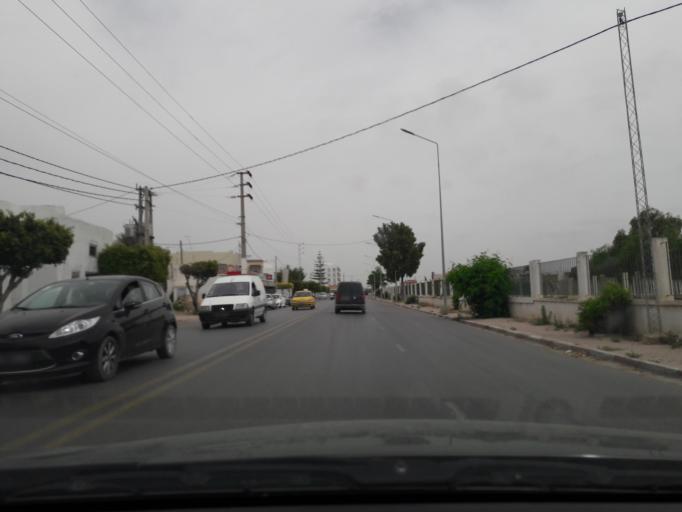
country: TN
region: Safaqis
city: Al Qarmadah
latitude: 34.7877
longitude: 10.7602
